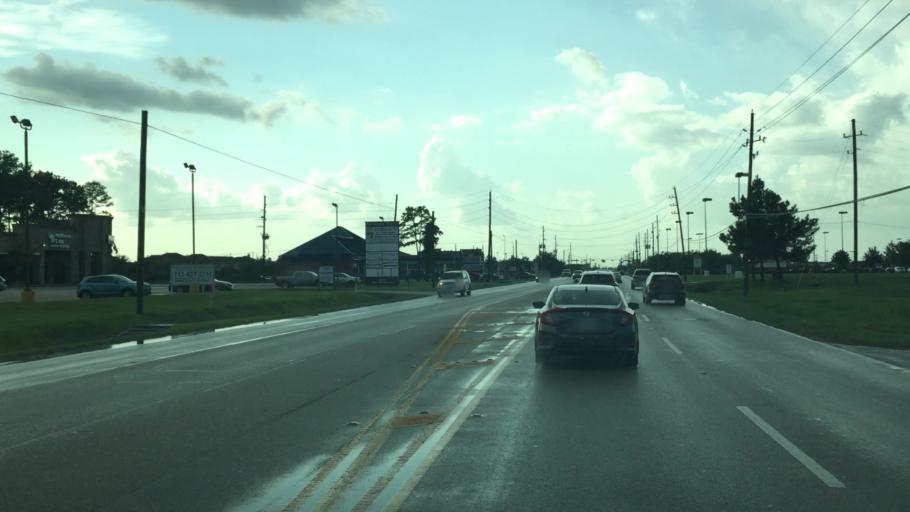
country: US
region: Texas
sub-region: Harris County
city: Spring
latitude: 30.0681
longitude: -95.5070
